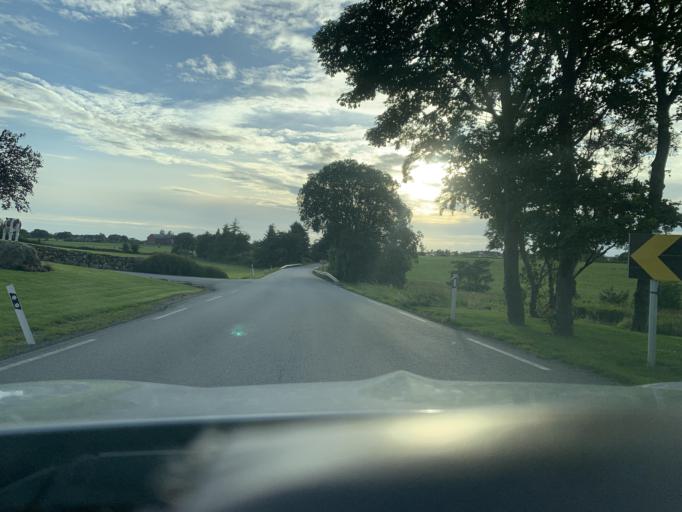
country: NO
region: Rogaland
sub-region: Time
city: Bryne
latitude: 58.7026
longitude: 5.7021
